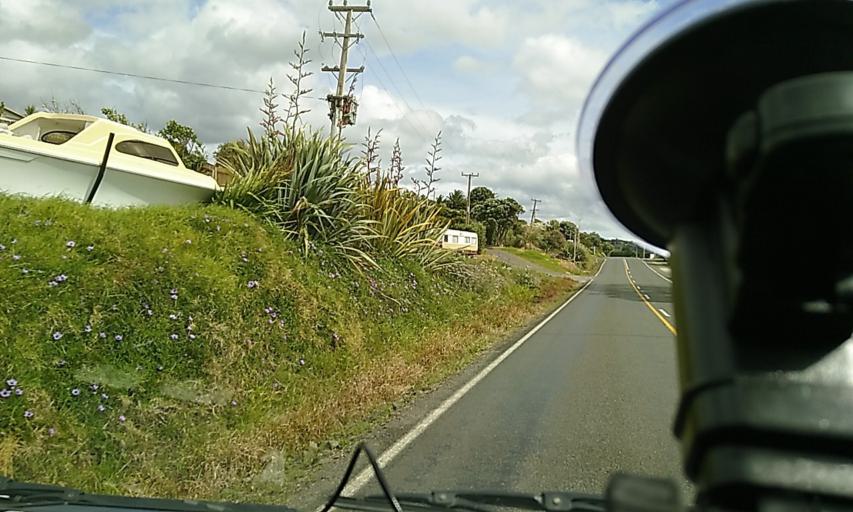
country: NZ
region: Northland
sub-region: Far North District
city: Ahipara
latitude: -35.5127
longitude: 173.3890
